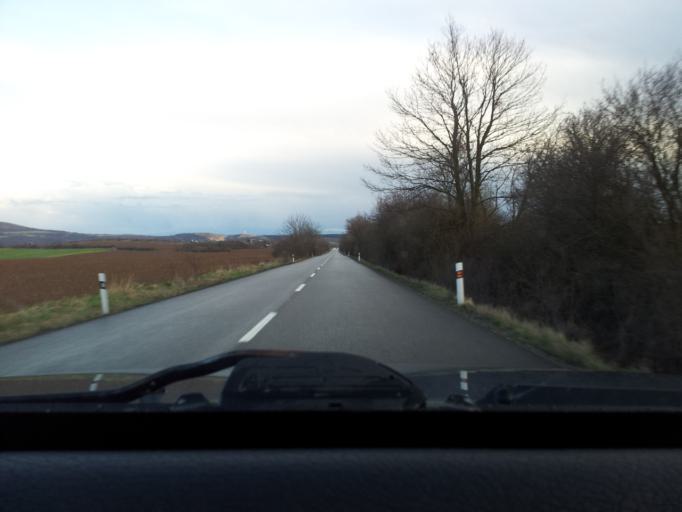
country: SK
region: Nitriansky
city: Tlmace
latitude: 48.3386
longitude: 18.4881
